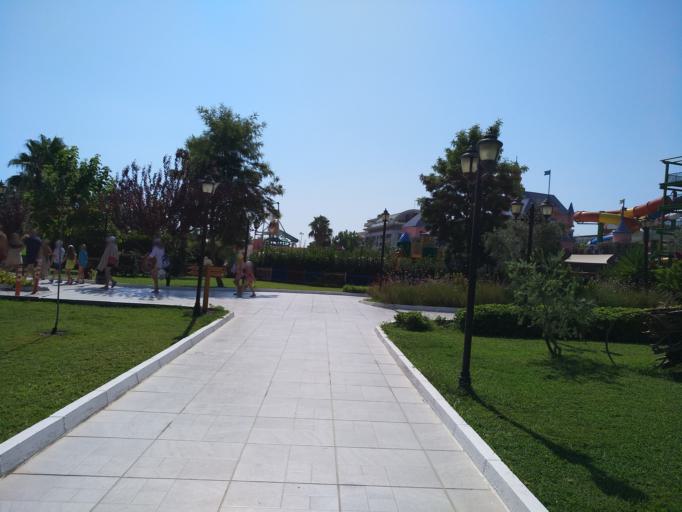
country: TR
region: Antalya
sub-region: Kemer
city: Goeynuek
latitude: 36.6659
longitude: 30.5597
